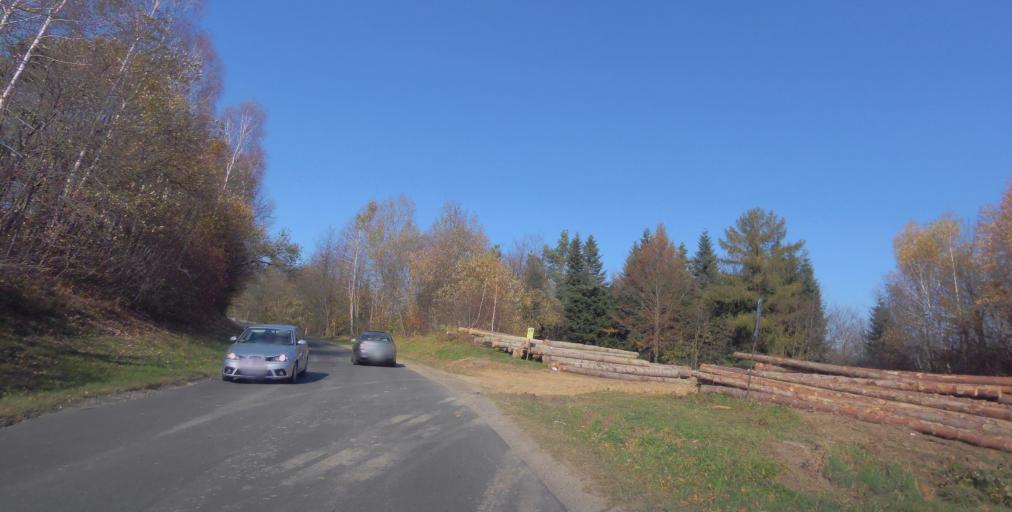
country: PL
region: Subcarpathian Voivodeship
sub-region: Powiat leski
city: Polanczyk
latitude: 49.3418
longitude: 22.4181
